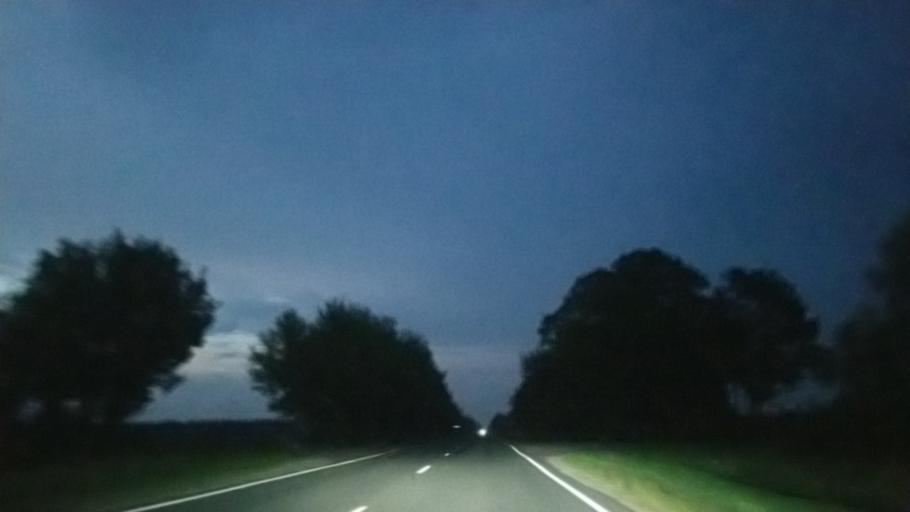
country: PL
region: Lublin Voivodeship
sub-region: Powiat bialski
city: Koden
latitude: 51.8867
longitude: 23.6489
